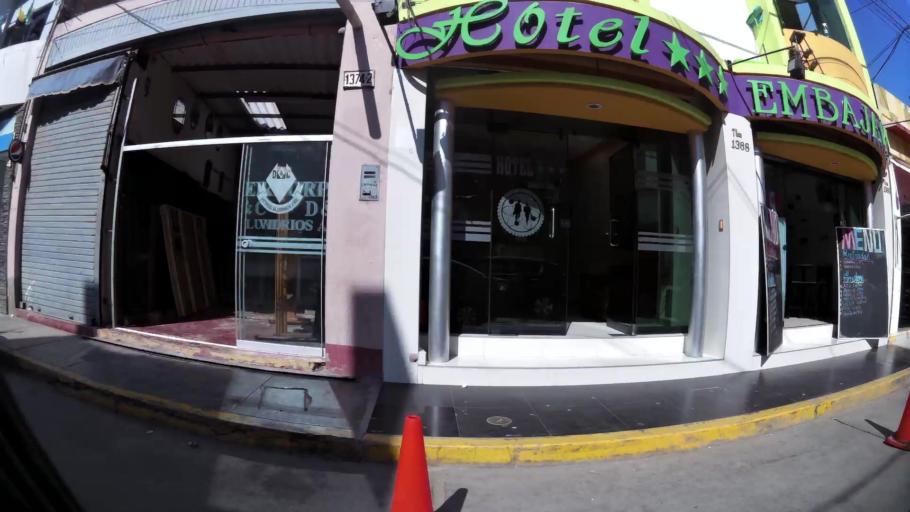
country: PE
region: Lambayeque
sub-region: Provincia de Chiclayo
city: Santa Rosa
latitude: -6.7671
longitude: -79.8369
